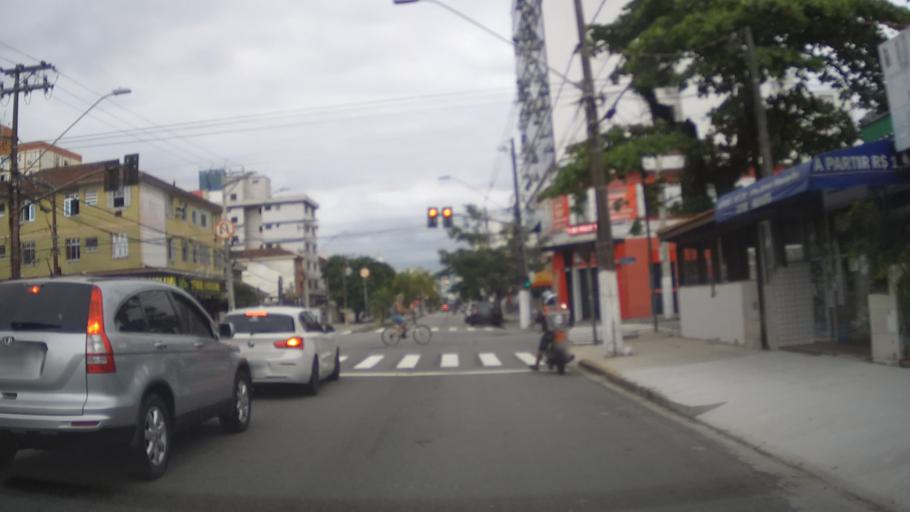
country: BR
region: Sao Paulo
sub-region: Santos
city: Santos
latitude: -23.9726
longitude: -46.3069
